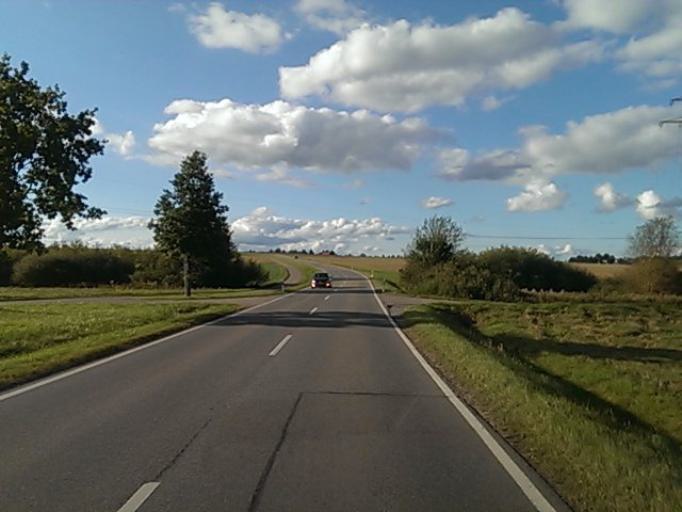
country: DE
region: Baden-Wuerttemberg
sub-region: Freiburg Region
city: Dunningen
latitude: 48.2279
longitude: 8.4998
